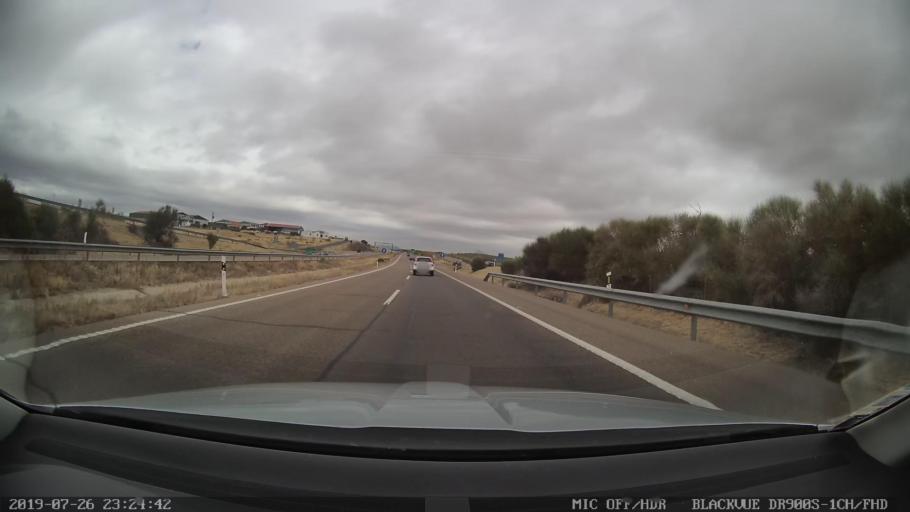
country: ES
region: Extremadura
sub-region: Provincia de Caceres
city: Escurial
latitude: 39.1761
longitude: -5.8972
